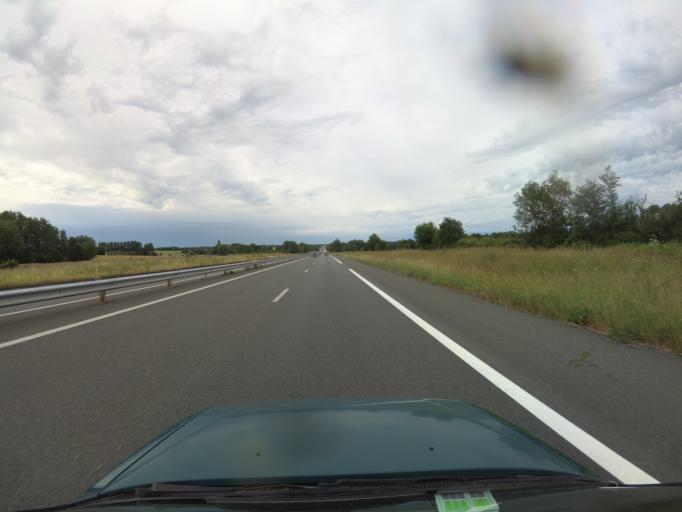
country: FR
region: Pays de la Loire
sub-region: Departement de la Vendee
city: Saint-Martin-des-Noyers
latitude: 46.7018
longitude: -1.1565
